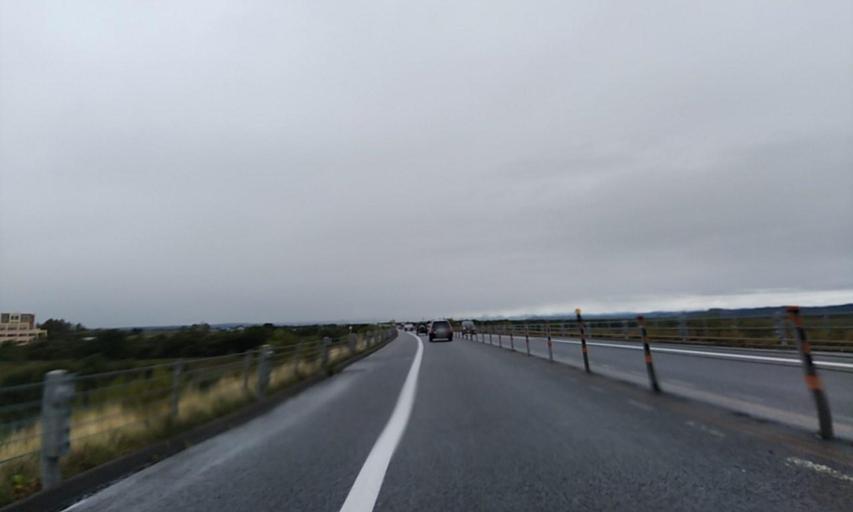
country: JP
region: Hokkaido
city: Kushiro
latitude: 43.0361
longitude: 144.3624
